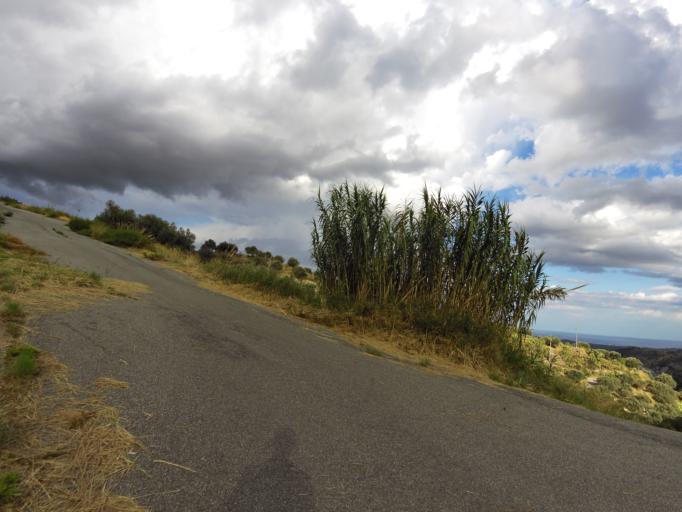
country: IT
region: Calabria
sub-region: Provincia di Reggio Calabria
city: Stilo
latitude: 38.4788
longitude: 16.4722
